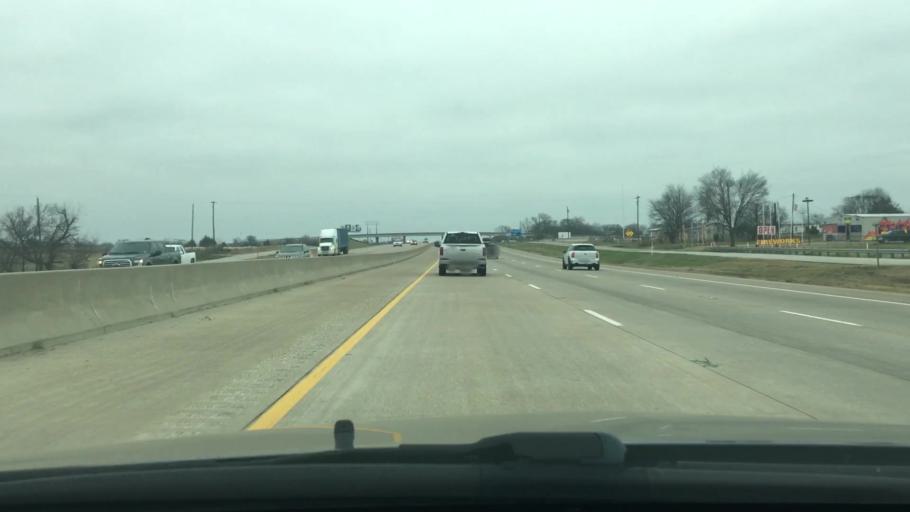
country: US
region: Texas
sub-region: Ellis County
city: Ennis
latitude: 32.2614
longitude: -96.5059
